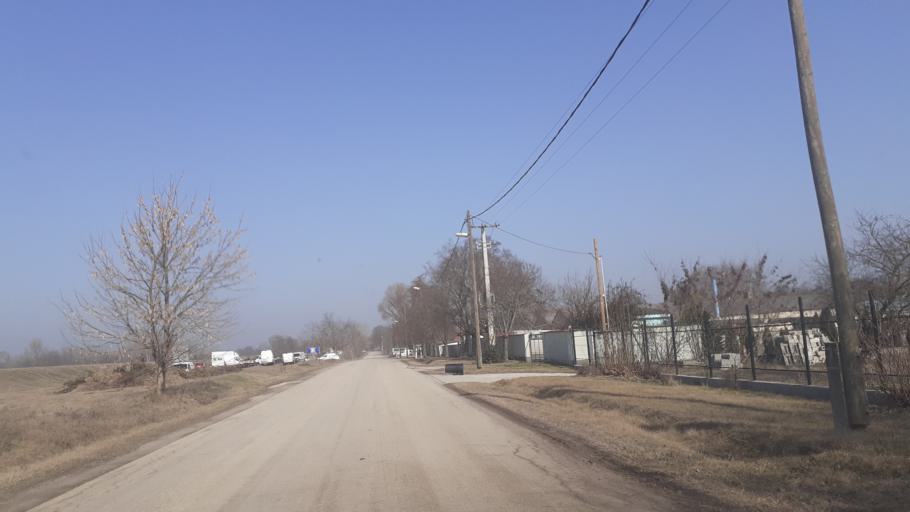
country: HU
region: Pest
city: Domsod
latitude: 47.0743
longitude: 19.0010
